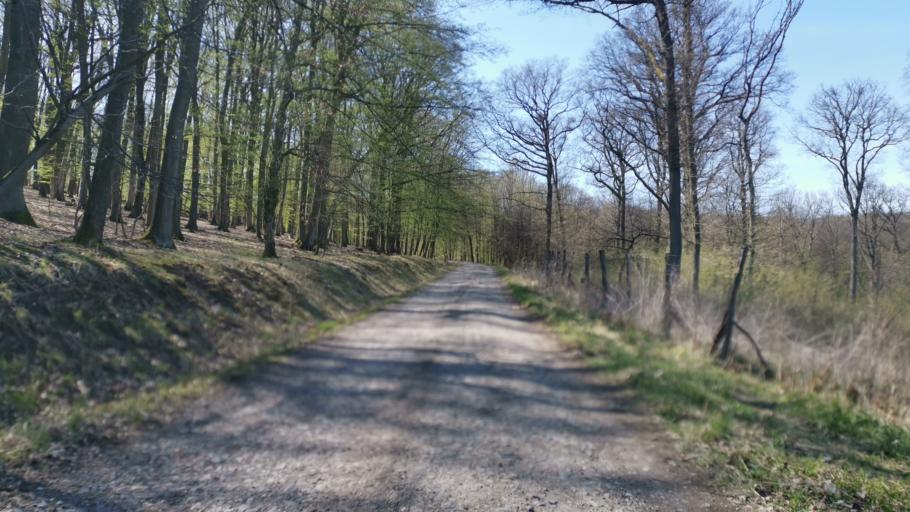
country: SK
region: Trnavsky
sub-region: Okres Skalica
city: Skalica
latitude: 48.7396
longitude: 17.2631
